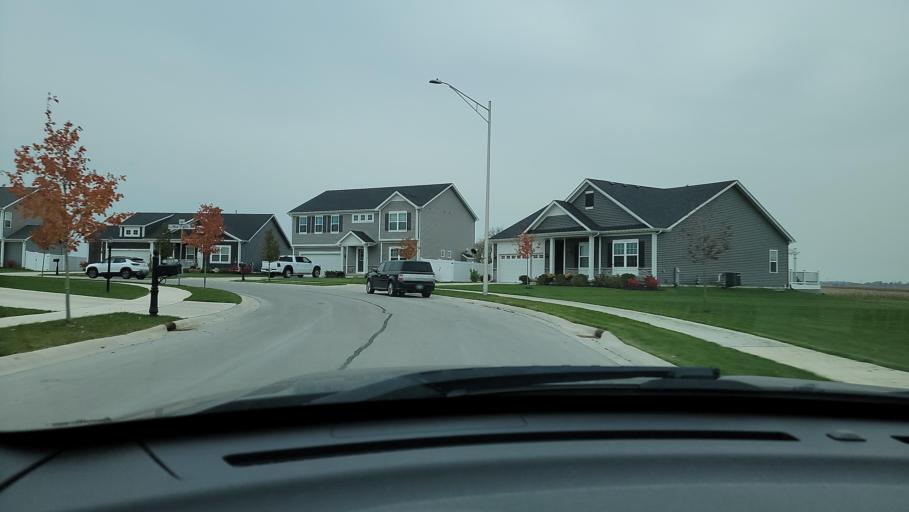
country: US
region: Indiana
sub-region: Porter County
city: Portage
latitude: 41.5441
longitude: -87.1708
